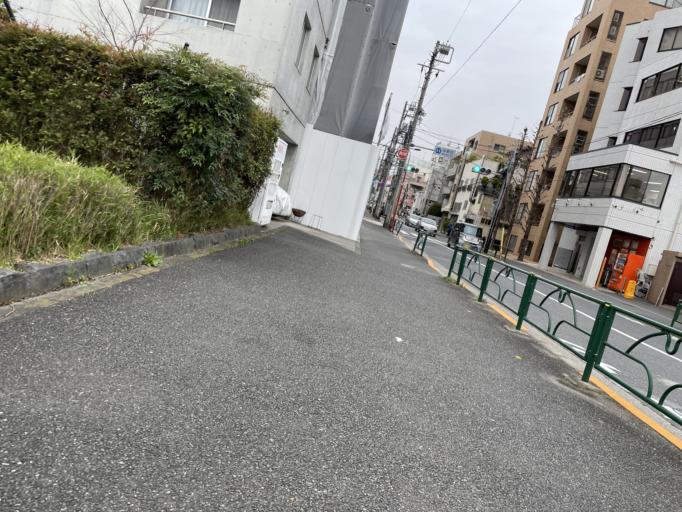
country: JP
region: Tokyo
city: Tokyo
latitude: 35.7016
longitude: 139.6874
